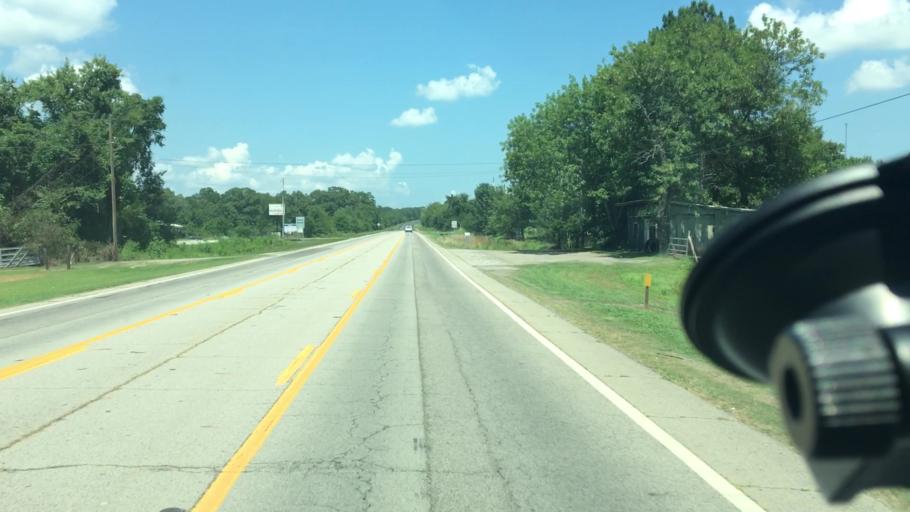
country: US
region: Arkansas
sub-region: Sebastian County
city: Lavaca
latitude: 35.2962
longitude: -94.1469
